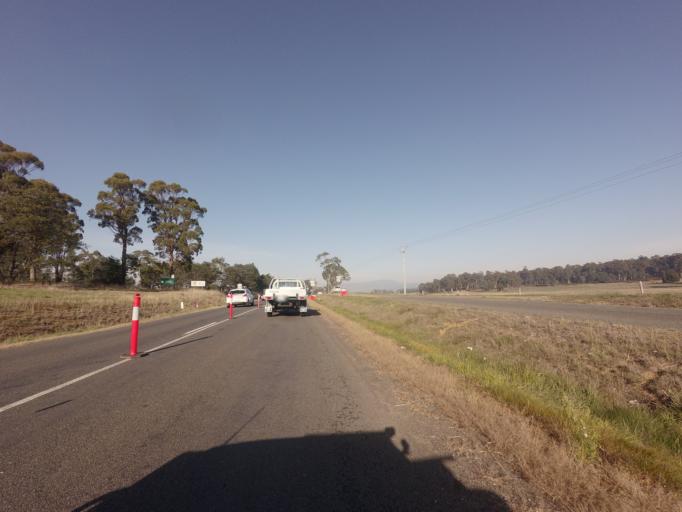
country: AU
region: Tasmania
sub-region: Northern Midlands
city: Longford
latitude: -41.5545
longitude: 146.9882
